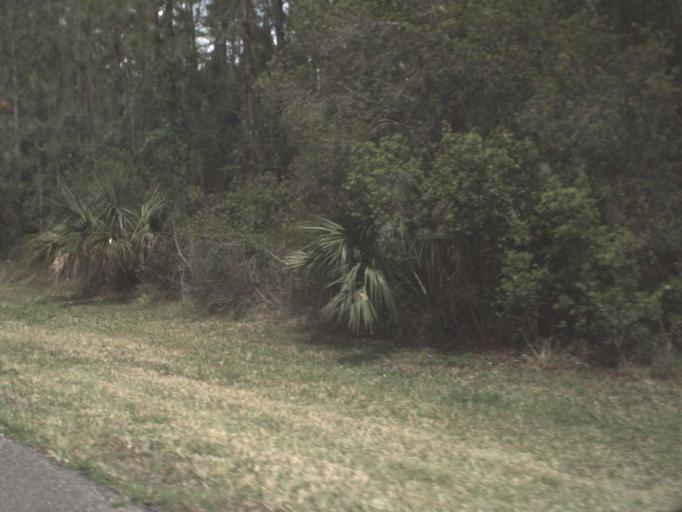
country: US
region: Florida
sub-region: Flagler County
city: Bunnell
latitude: 29.3726
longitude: -81.3116
